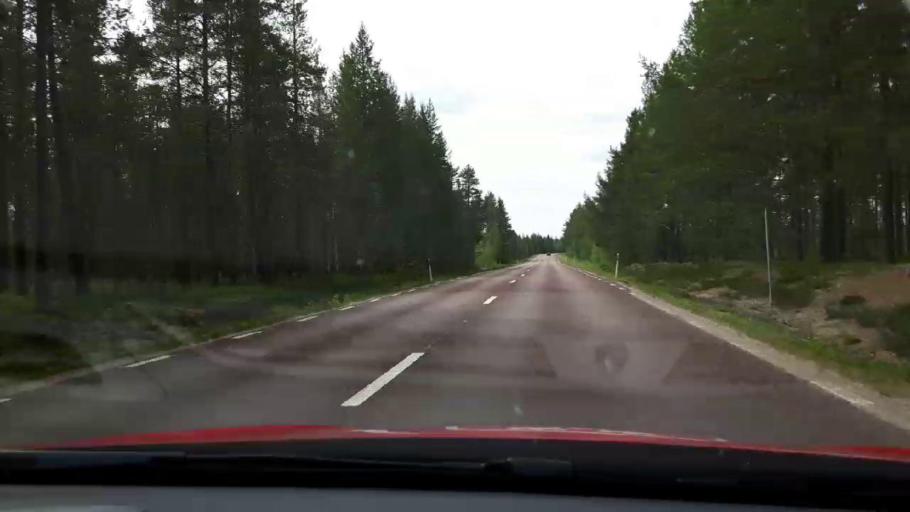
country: SE
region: Jaemtland
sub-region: Harjedalens Kommun
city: Sveg
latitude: 62.0578
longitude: 14.5680
